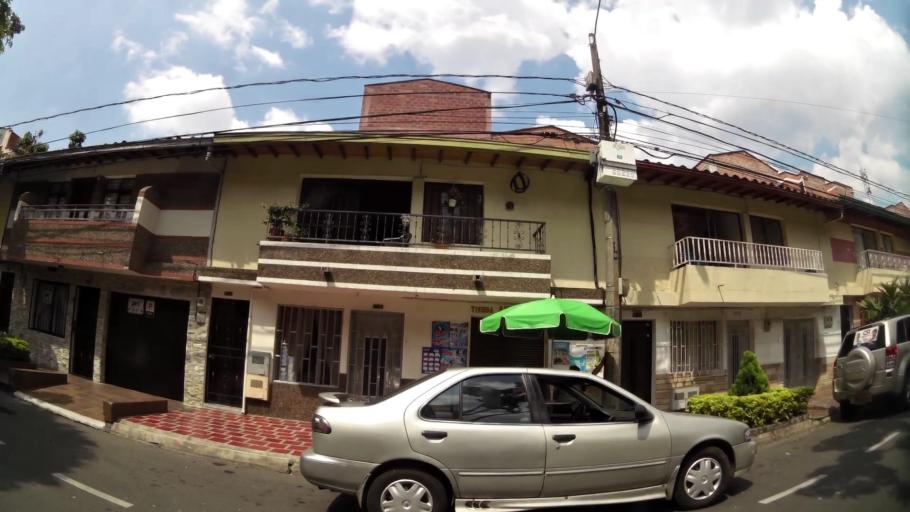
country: CO
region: Antioquia
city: Envigado
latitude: 6.1686
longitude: -75.5943
